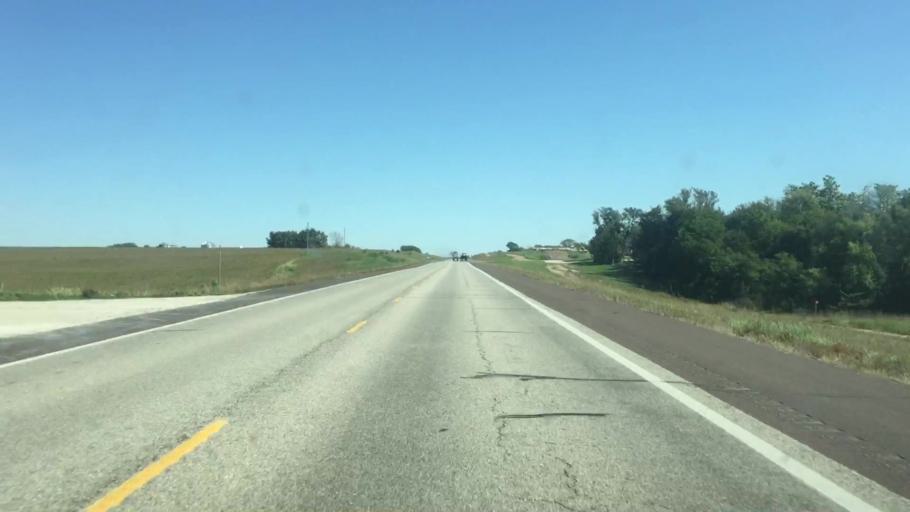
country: US
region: Kansas
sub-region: Nemaha County
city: Seneca
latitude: 39.8421
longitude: -96.2901
